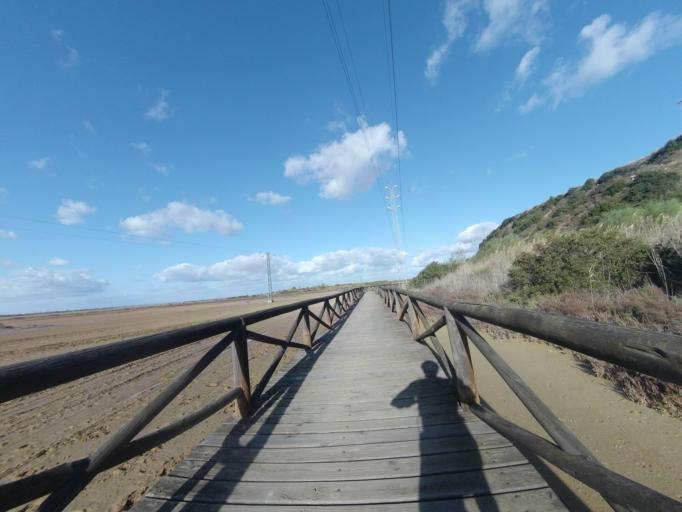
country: ES
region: Andalusia
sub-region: Provincia de Huelva
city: Palos de la Frontera
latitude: 37.2525
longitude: -6.8783
